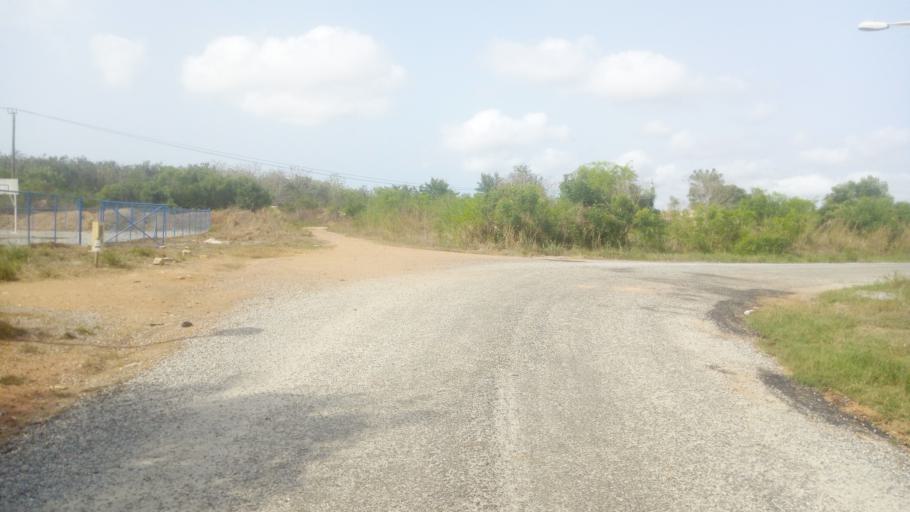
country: GH
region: Central
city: Winneba
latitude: 5.3793
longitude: -0.6216
